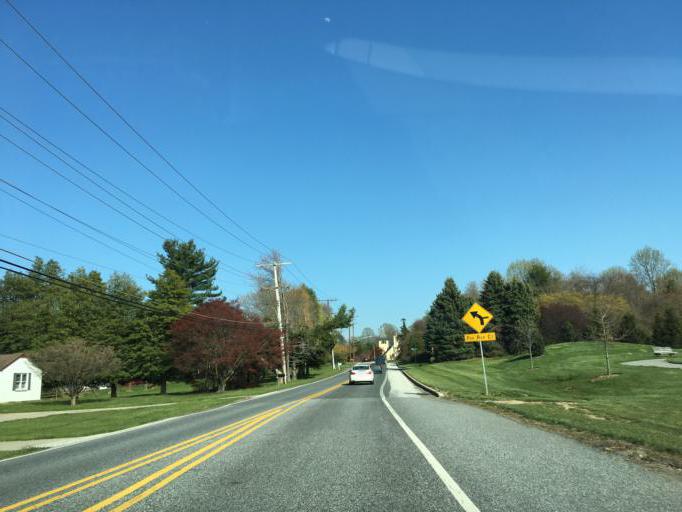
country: US
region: Maryland
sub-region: Baltimore County
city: Hunt Valley
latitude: 39.5136
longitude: -76.5532
